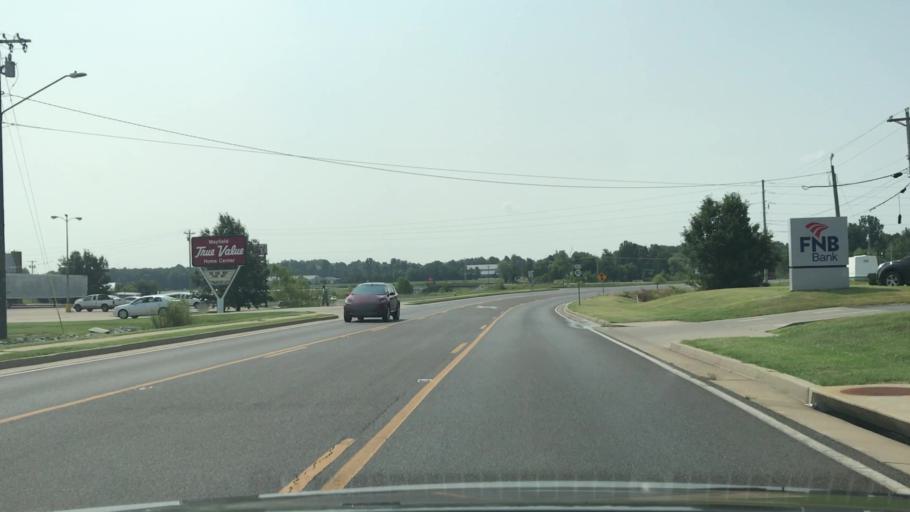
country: US
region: Kentucky
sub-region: Graves County
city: Mayfield
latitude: 36.7186
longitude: -88.6252
